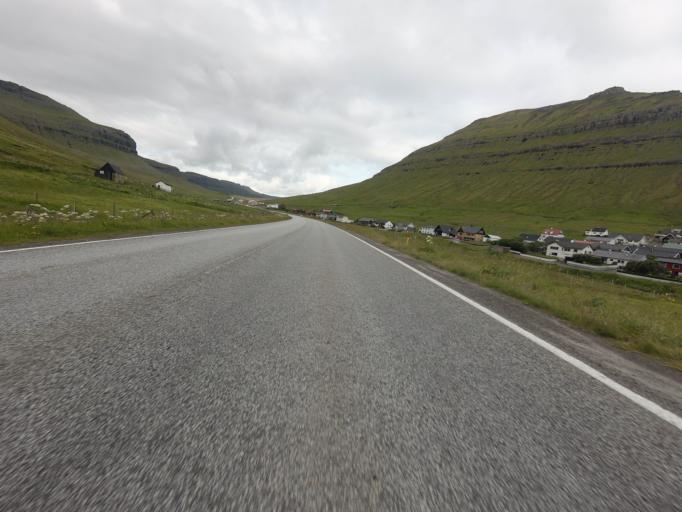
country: FO
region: Eysturoy
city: Eystur
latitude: 62.2002
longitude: -6.7489
